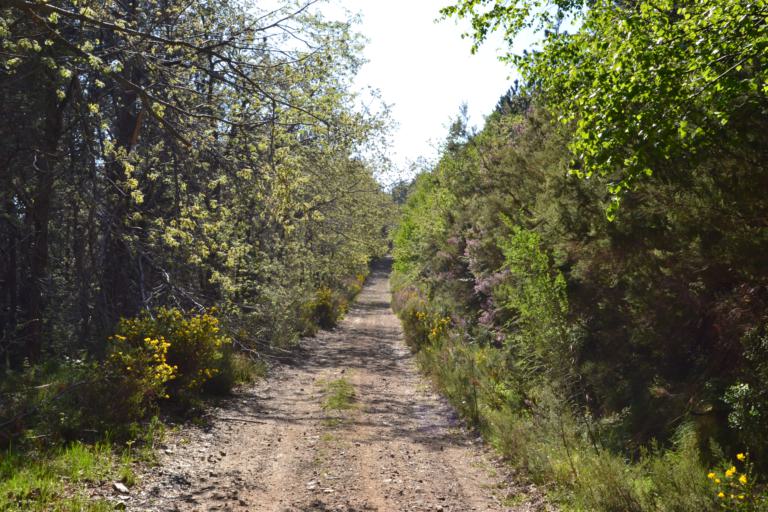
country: PT
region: Vila Real
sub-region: Mesao Frio
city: Mesao Frio
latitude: 41.2741
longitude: -7.9084
